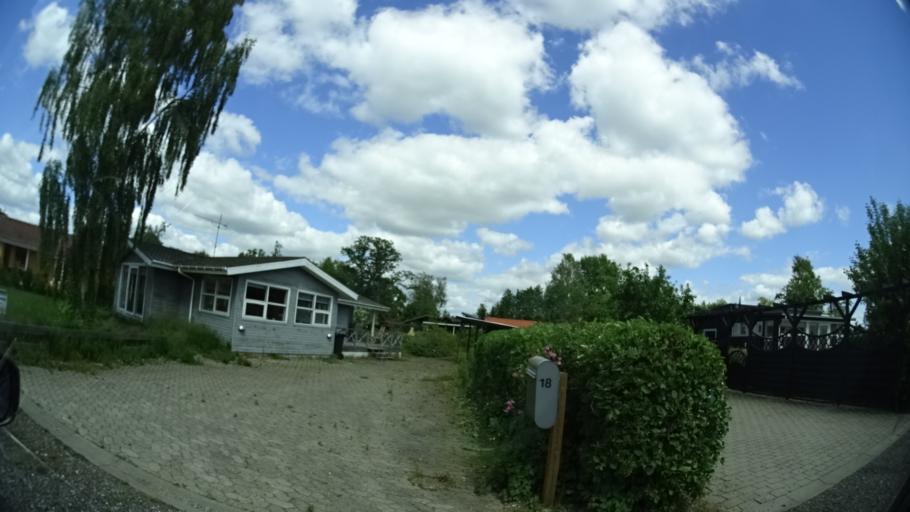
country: DK
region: Central Jutland
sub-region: Syddjurs Kommune
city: Ronde
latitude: 56.2948
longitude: 10.4195
